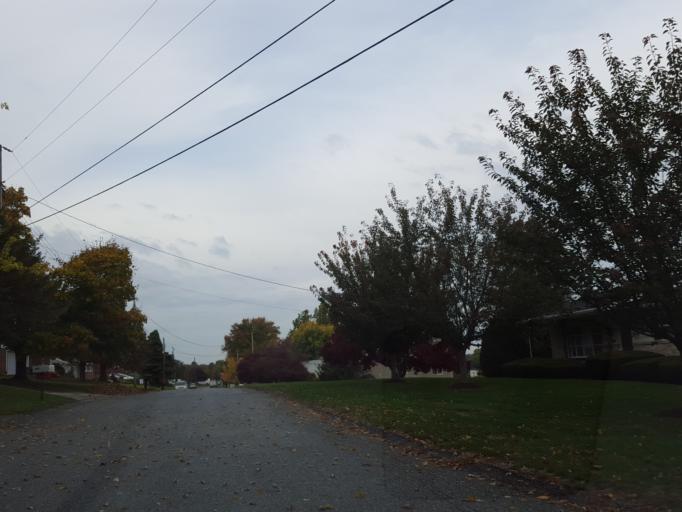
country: US
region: Pennsylvania
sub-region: York County
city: Spry
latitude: 39.9298
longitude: -76.6645
